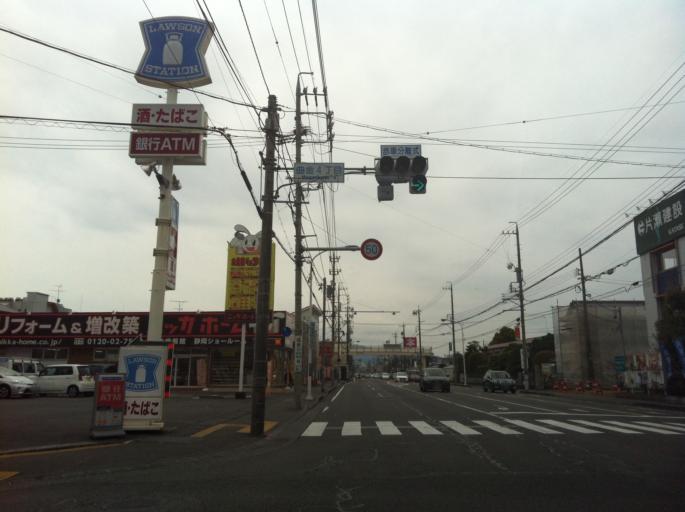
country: JP
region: Shizuoka
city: Shizuoka-shi
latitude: 34.9785
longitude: 138.4094
